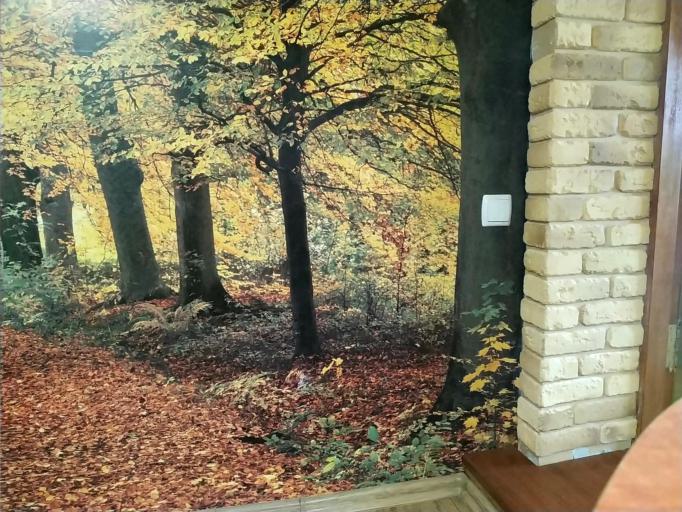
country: RU
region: Smolensk
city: Dorogobuzh
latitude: 54.8442
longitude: 33.3263
